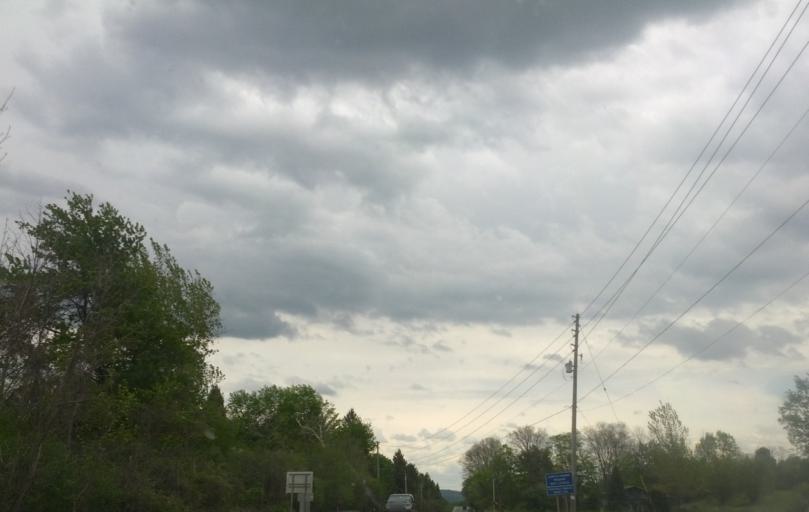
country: US
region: New York
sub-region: Onondaga County
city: Fayetteville
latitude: 42.9924
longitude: -76.0299
